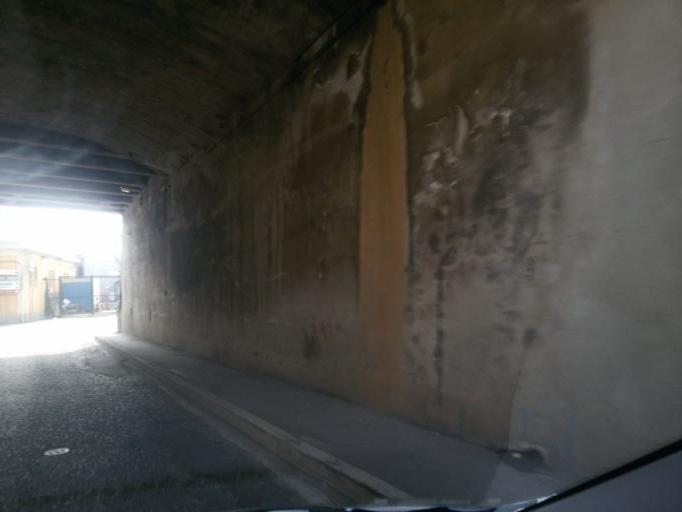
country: IT
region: Liguria
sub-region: Provincia di Genova
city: San Teodoro
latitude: 44.4159
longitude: 8.8778
